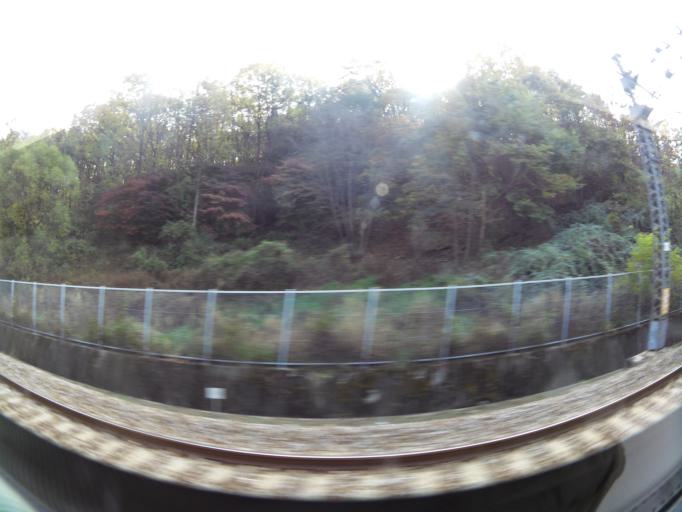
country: KR
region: Daejeon
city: Daejeon
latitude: 36.3354
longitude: 127.4882
